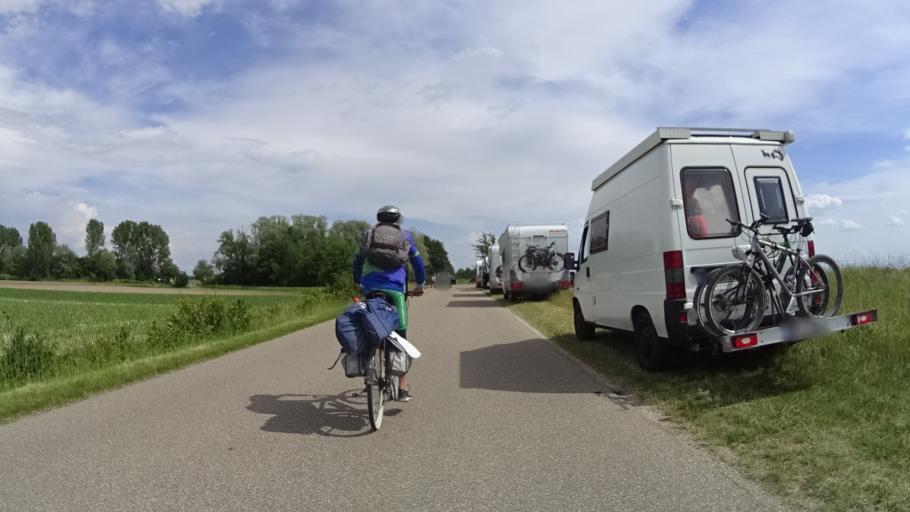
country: DE
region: Bavaria
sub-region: Upper Palatinate
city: Wiesent
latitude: 49.0077
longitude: 12.3328
